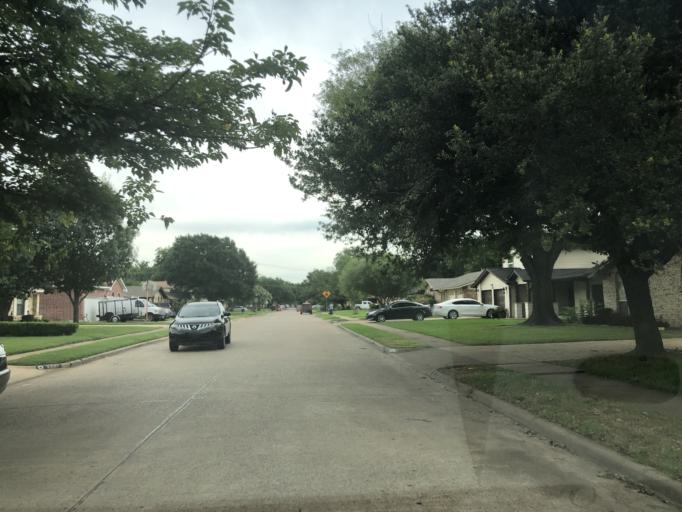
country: US
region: Texas
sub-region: Dallas County
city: Irving
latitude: 32.7867
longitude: -96.9752
